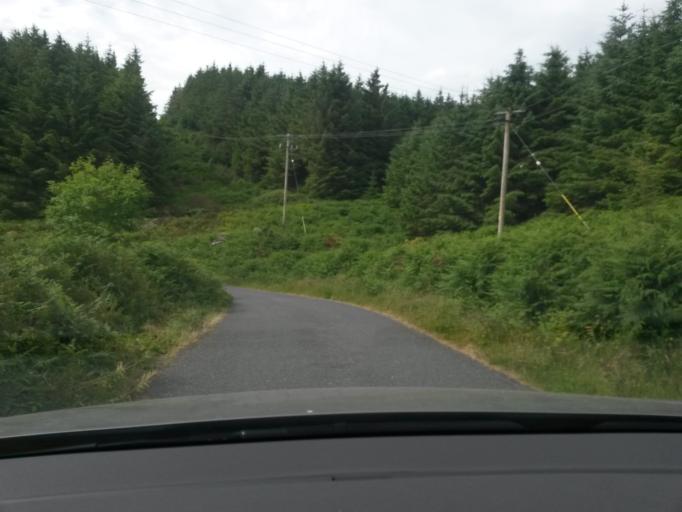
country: IE
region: Leinster
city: Ballinteer
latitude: 53.1878
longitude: -6.2881
